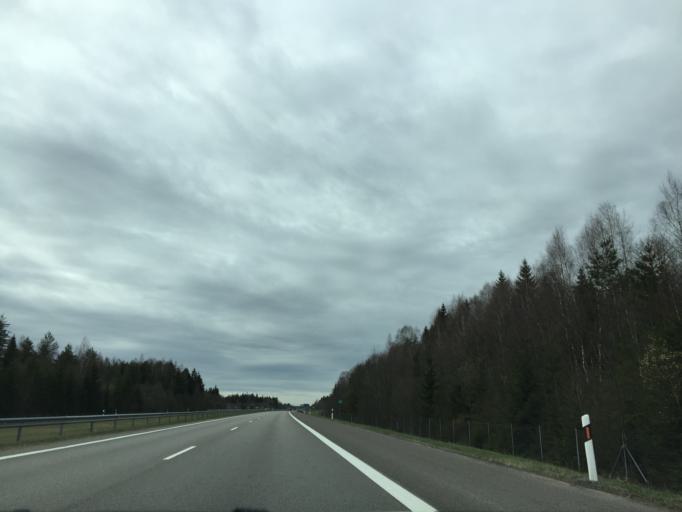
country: LT
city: Rietavas
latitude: 55.6171
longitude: 22.0066
